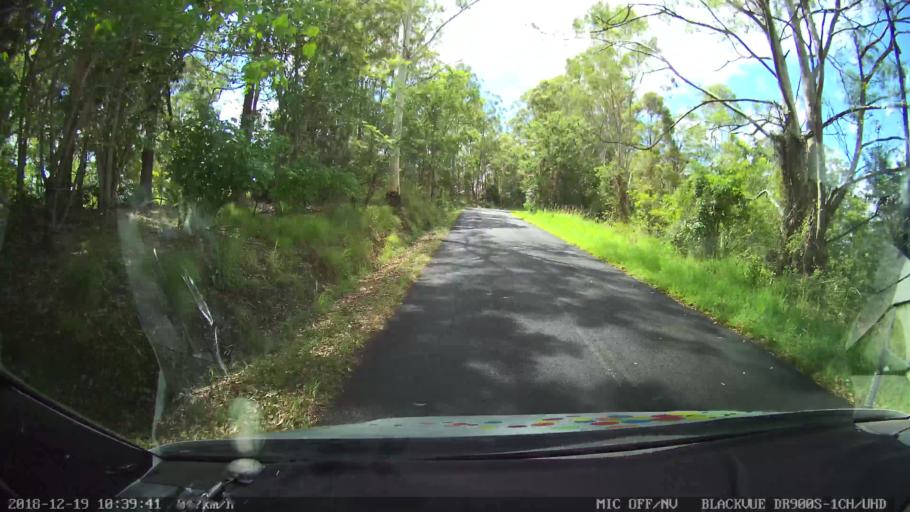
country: AU
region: New South Wales
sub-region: Lismore Municipality
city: Nimbin
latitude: -28.5819
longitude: 153.1560
